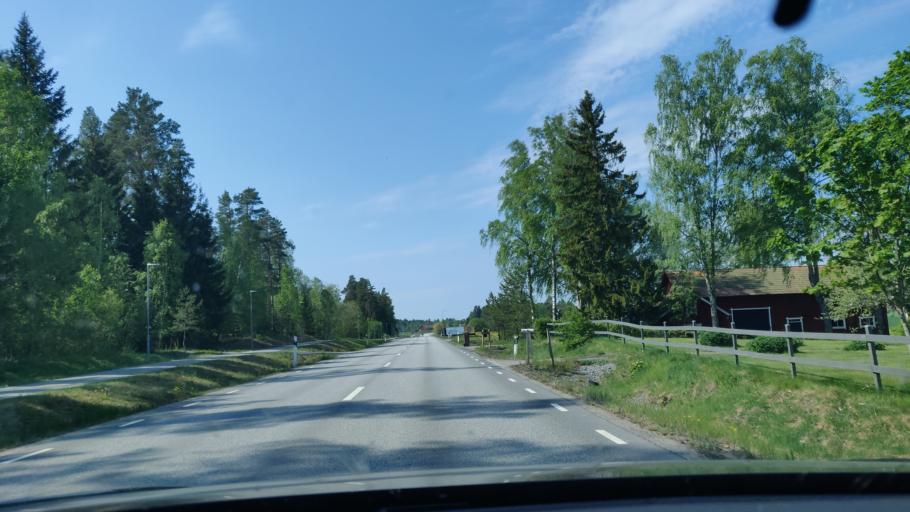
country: SE
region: Uppsala
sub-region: Heby Kommun
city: OEstervala
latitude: 60.1685
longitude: 17.1895
